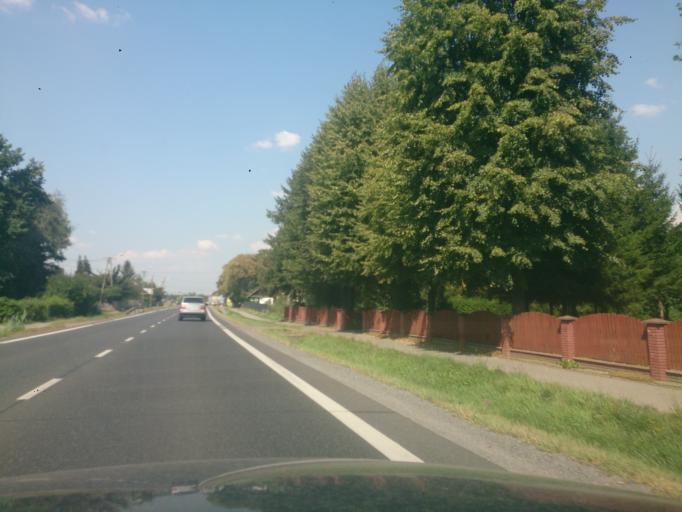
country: PL
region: Subcarpathian Voivodeship
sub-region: Powiat kolbuszowski
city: Kolbuszowa
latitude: 50.2298
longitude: 21.7901
